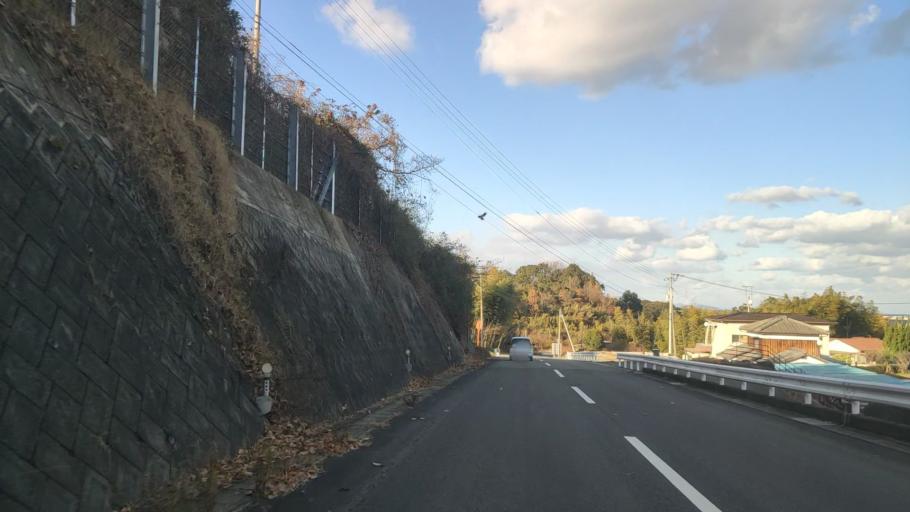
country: JP
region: Ehime
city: Saijo
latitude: 33.8864
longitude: 133.1291
